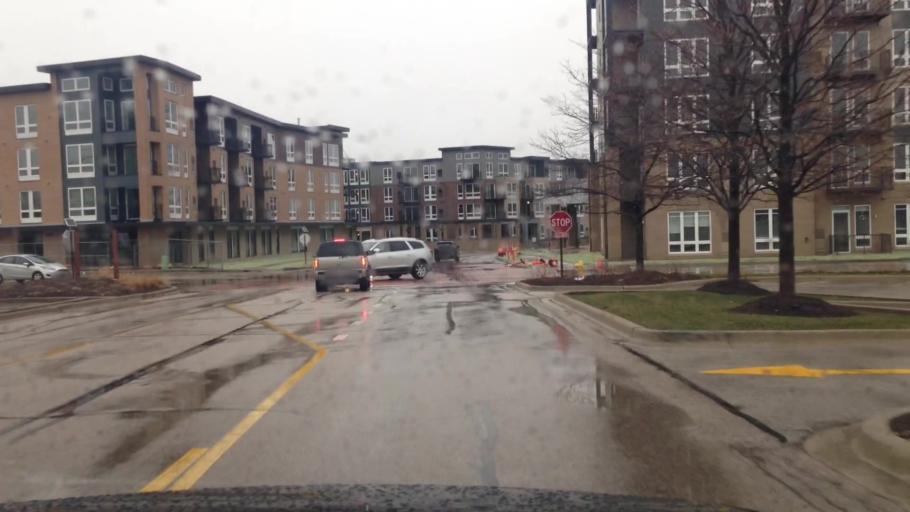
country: US
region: Illinois
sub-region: DuPage County
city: Downers Grove
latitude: 41.8424
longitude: -88.0068
